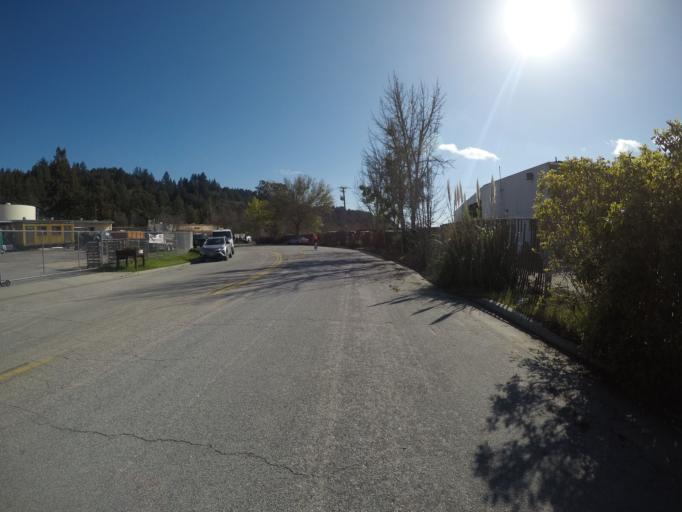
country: US
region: California
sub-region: Santa Cruz County
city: Scotts Valley
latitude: 37.0543
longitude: -122.0100
